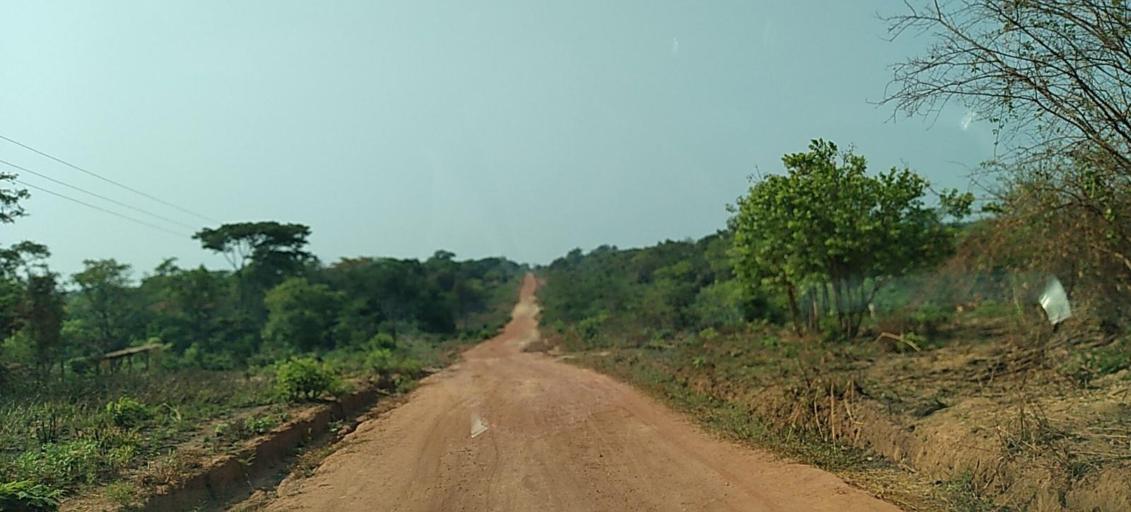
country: ZM
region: Copperbelt
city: Chingola
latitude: -12.9072
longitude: 27.3714
